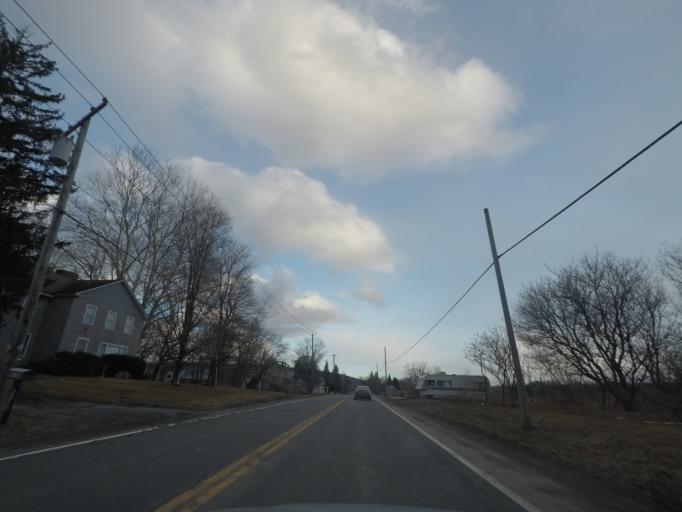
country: US
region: New York
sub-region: Herkimer County
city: Frankfort
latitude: 43.0570
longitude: -75.0798
